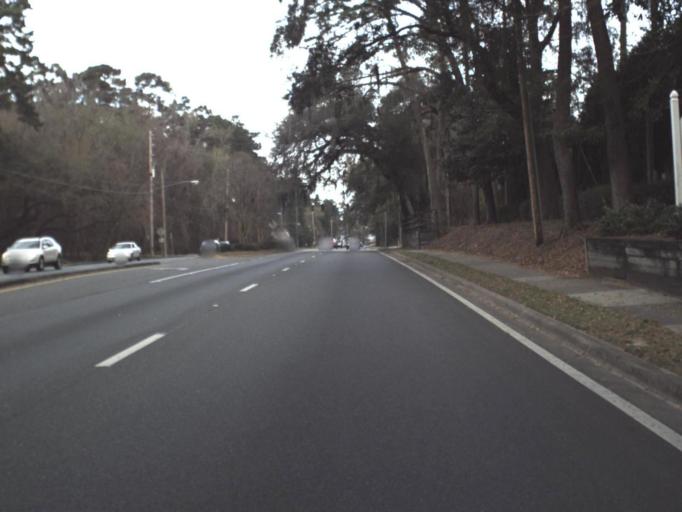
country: US
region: Florida
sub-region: Leon County
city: Tallahassee
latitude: 30.4915
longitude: -84.2546
